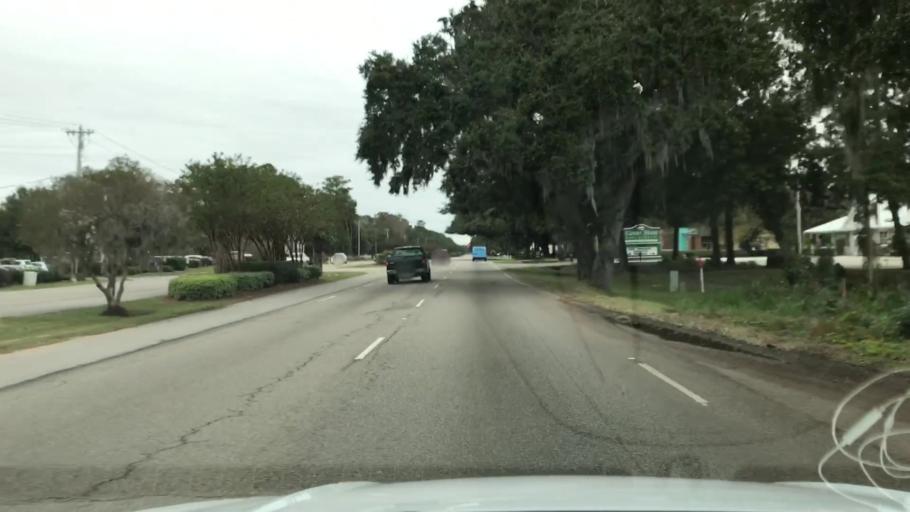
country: US
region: South Carolina
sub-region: Georgetown County
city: Murrells Inlet
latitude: 33.4865
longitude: -79.0940
